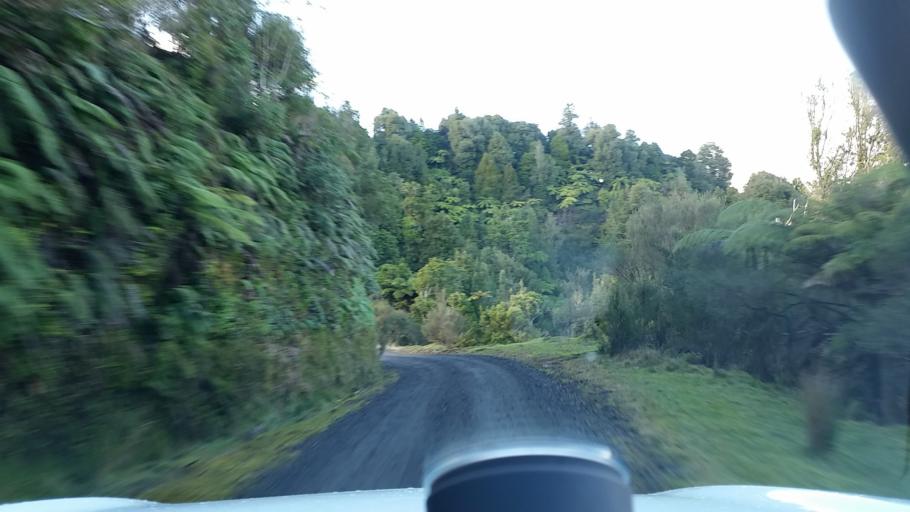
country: NZ
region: Taranaki
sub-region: South Taranaki District
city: Eltham
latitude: -39.4270
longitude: 174.5590
